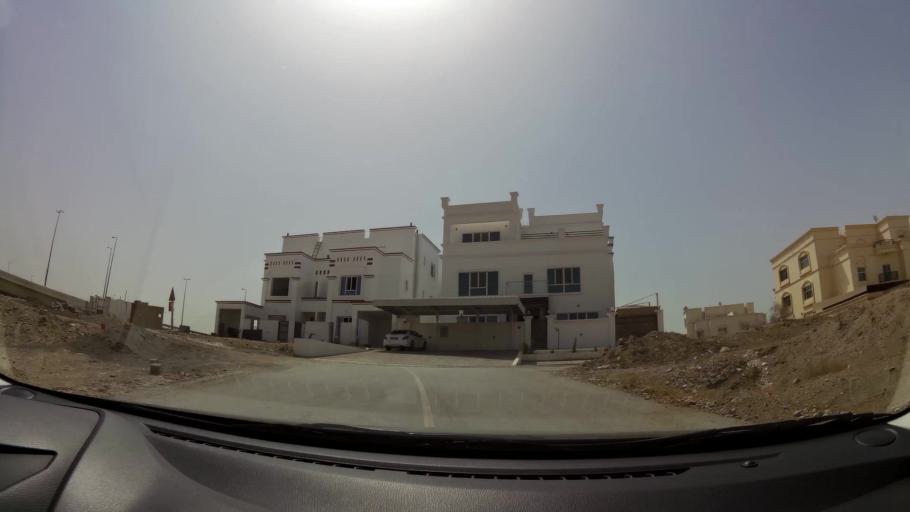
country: OM
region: Muhafazat Masqat
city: Bawshar
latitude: 23.5666
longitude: 58.3824
